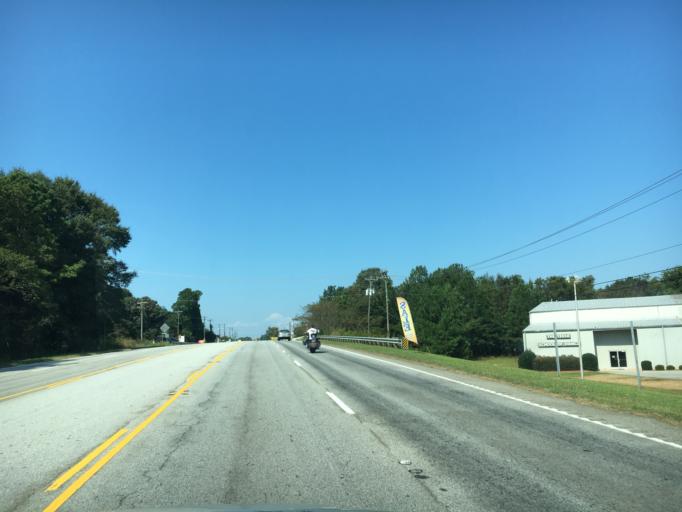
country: US
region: South Carolina
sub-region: Spartanburg County
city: Fairforest
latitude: 34.9377
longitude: -82.0264
